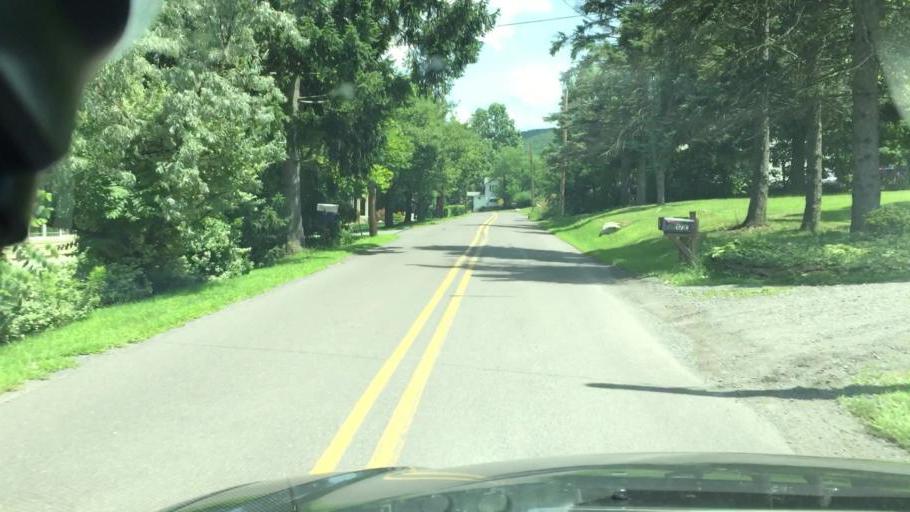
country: US
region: Pennsylvania
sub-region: Luzerne County
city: Harleigh
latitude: 41.0075
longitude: -75.9660
